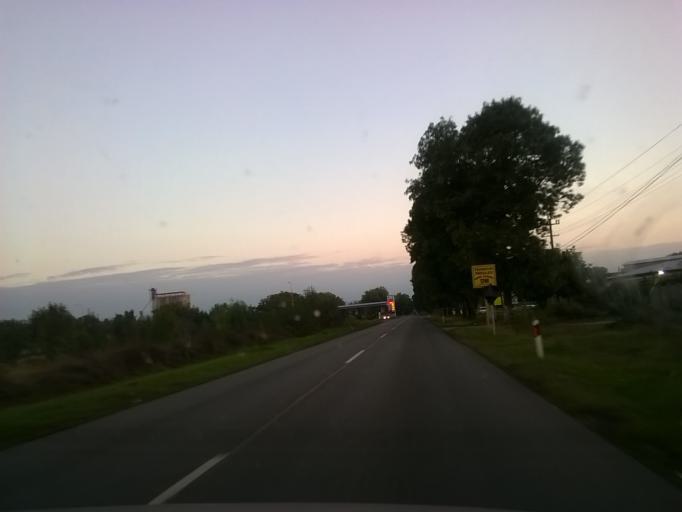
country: RS
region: Autonomna Pokrajina Vojvodina
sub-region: Juznobanatski Okrug
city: Pancevo
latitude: 44.9155
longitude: 20.6329
